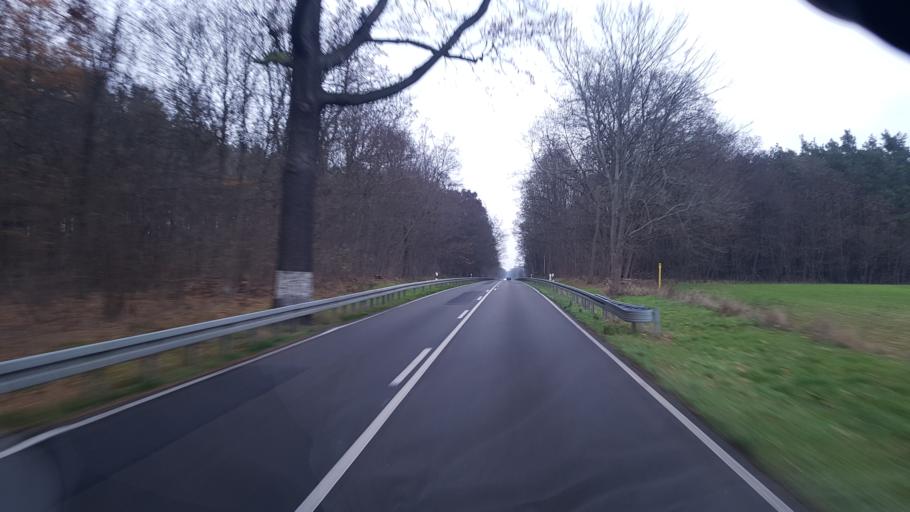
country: DE
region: Brandenburg
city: Tauer
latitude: 51.9026
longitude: 14.4727
